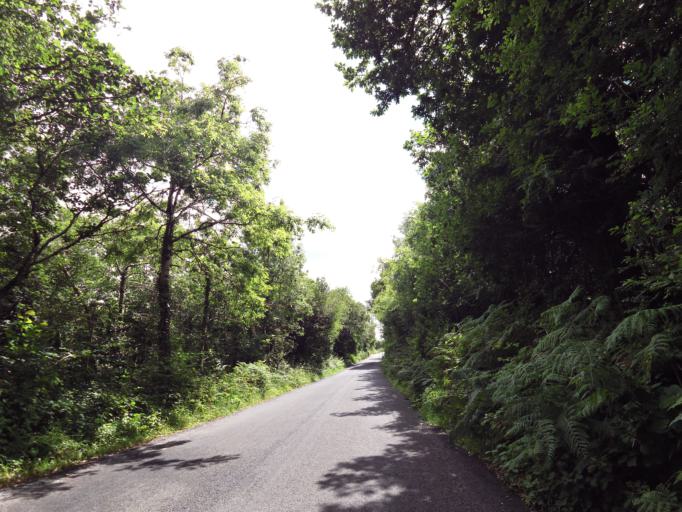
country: IE
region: Connaught
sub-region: County Galway
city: Oughterard
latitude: 53.4088
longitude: -9.3292
